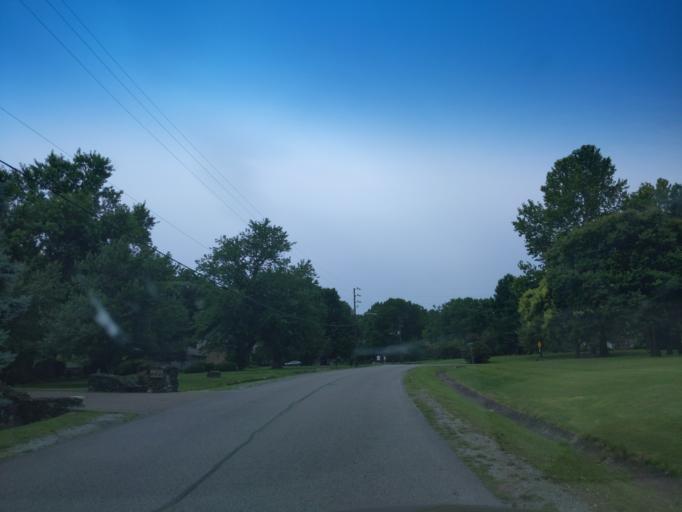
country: US
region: Tennessee
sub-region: Williamson County
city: Brentwood Estates
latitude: 36.0293
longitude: -86.7622
